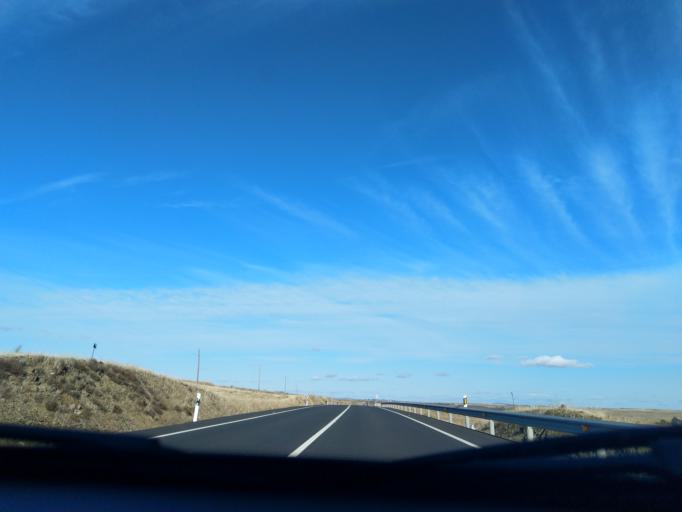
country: ES
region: Extremadura
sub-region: Provincia de Badajoz
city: Ahillones
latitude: 38.2653
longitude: -5.8506
